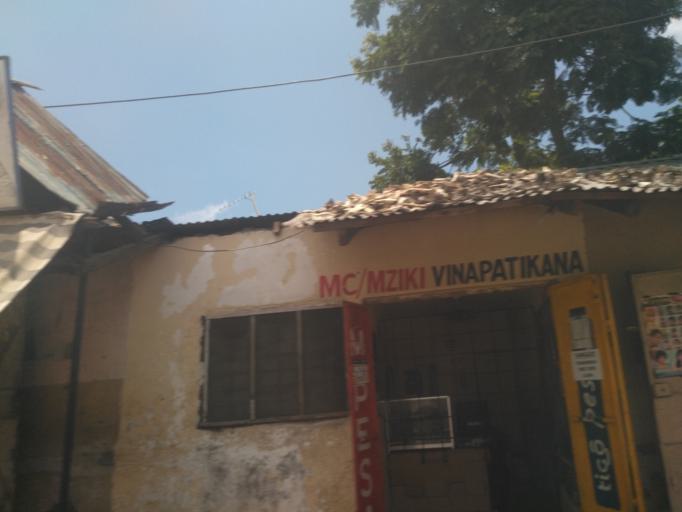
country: TZ
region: Dar es Salaam
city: Dar es Salaam
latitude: -6.8703
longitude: 39.2816
